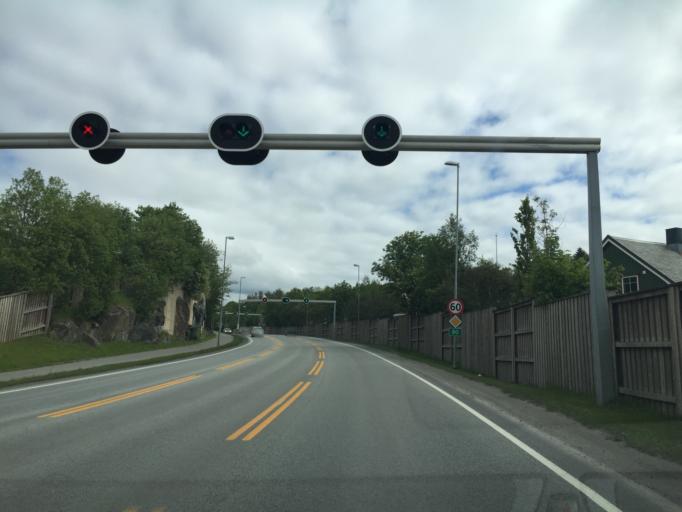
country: NO
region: Nordland
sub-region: Bodo
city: Bodo
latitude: 67.2758
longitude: 14.4425
